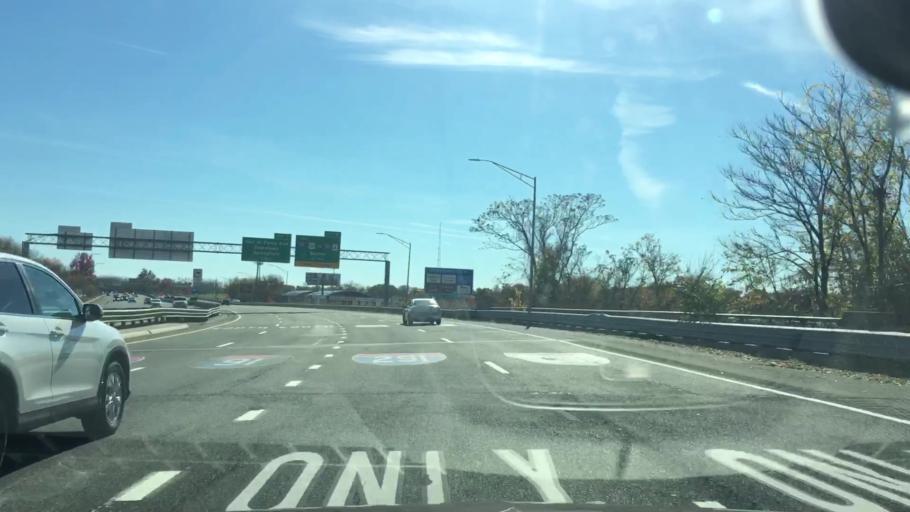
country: US
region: Massachusetts
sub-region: Hampden County
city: West Springfield
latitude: 42.1192
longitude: -72.6098
